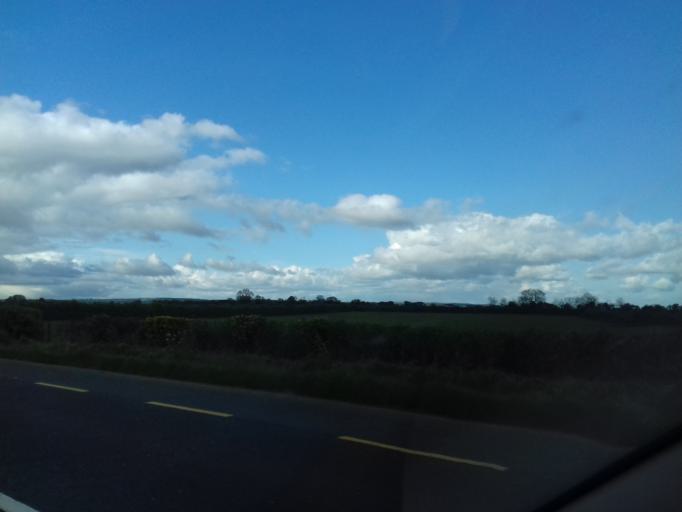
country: IE
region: Leinster
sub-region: Kilkenny
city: Kilkenny
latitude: 52.6050
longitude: -7.2427
